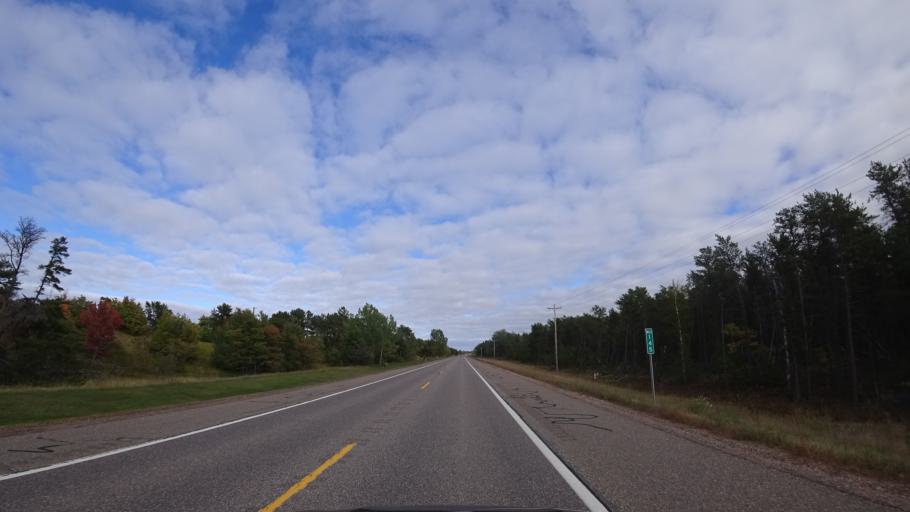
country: US
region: Michigan
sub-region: Marquette County
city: Harvey
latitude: 46.4899
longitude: -87.2037
